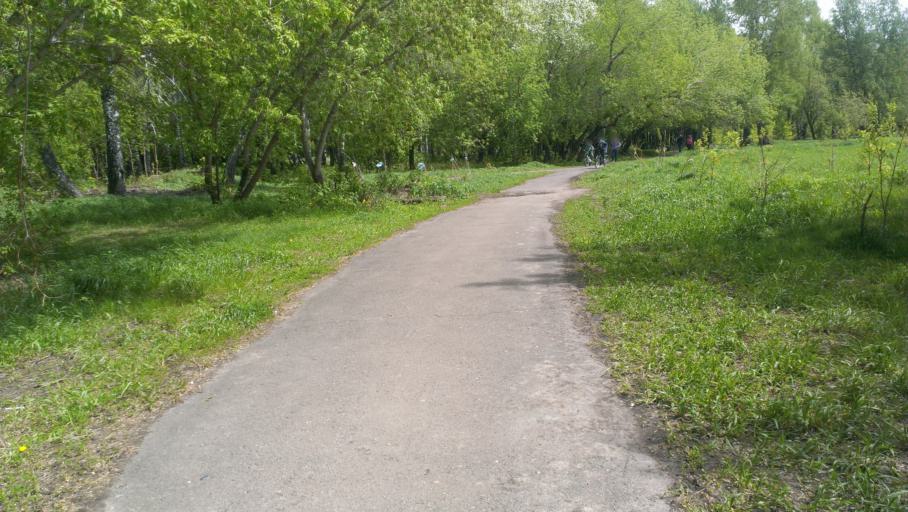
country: RU
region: Altai Krai
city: Novosilikatnyy
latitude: 53.3609
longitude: 83.6679
